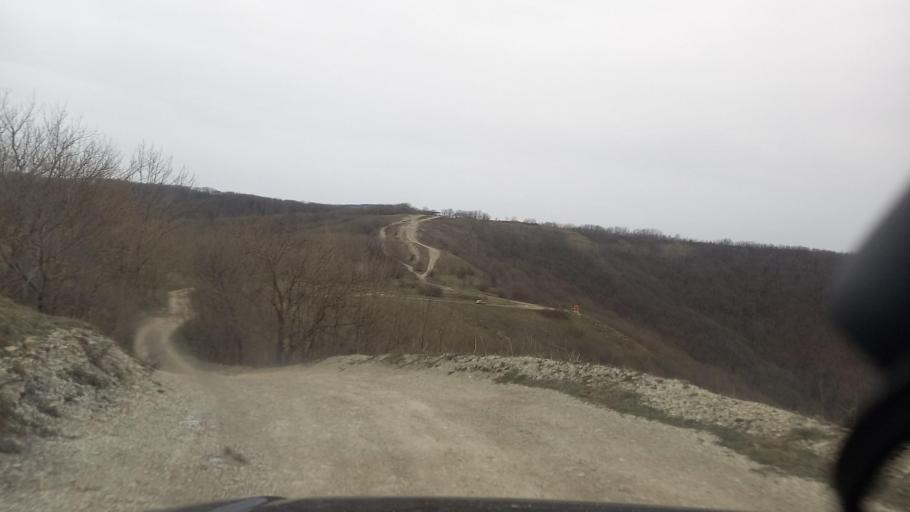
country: RU
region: Krasnodarskiy
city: Divnomorskoye
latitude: 44.6103
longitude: 38.2397
